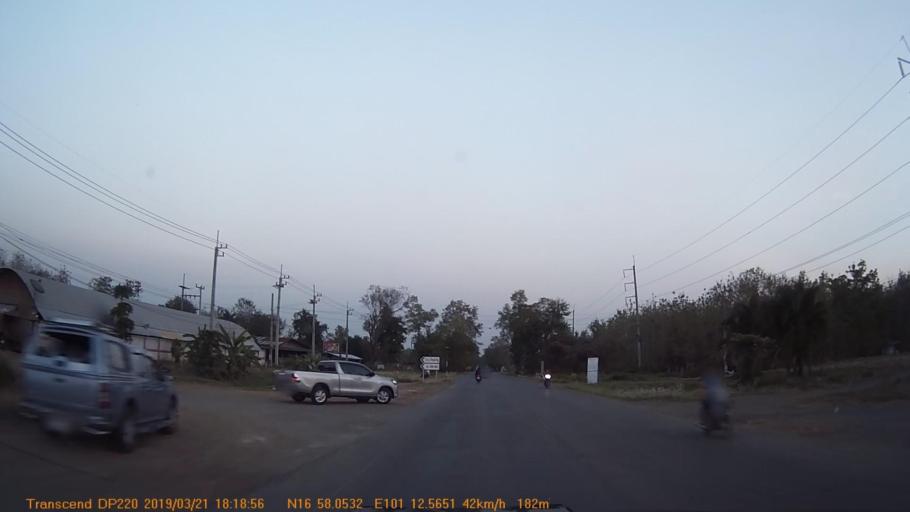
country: TH
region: Phetchabun
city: Lom Kao
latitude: 16.9674
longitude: 101.2095
